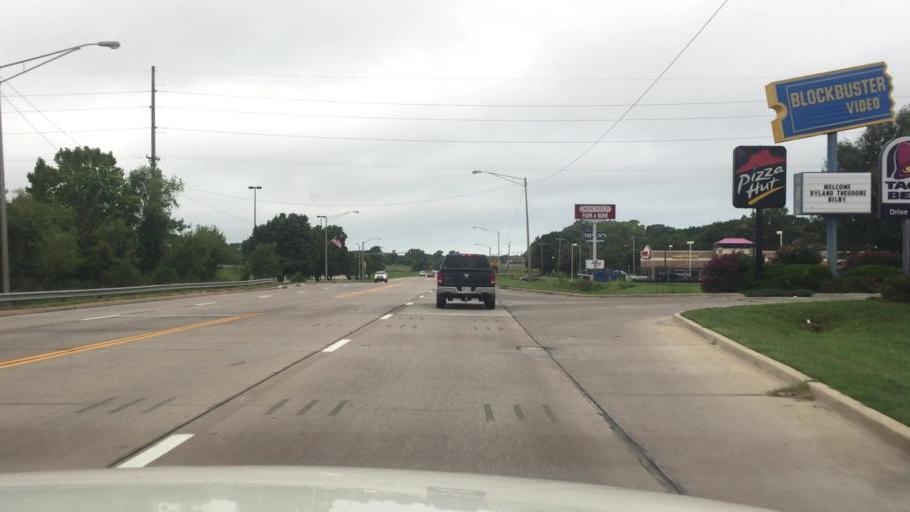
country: US
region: Kansas
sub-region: Montgomery County
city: Coffeyville
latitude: 37.0333
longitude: -95.6420
